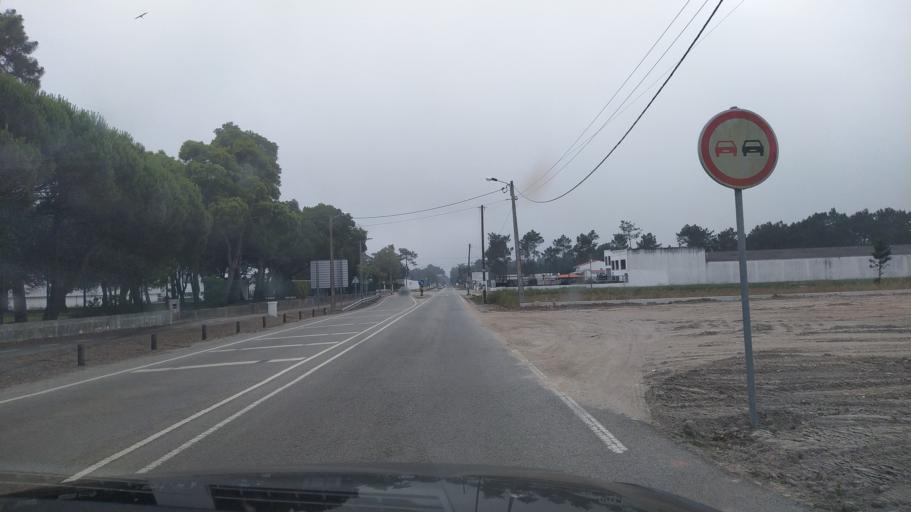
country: PT
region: Aveiro
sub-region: Ilhavo
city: Gafanha da Encarnacao
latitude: 40.6124
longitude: -8.7203
